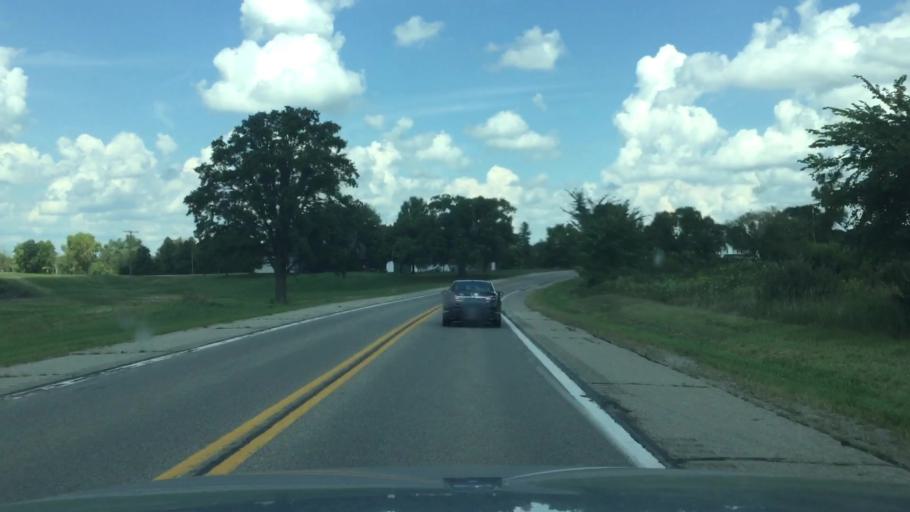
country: US
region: Michigan
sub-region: Lenawee County
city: Clinton
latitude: 42.1051
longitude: -83.8958
